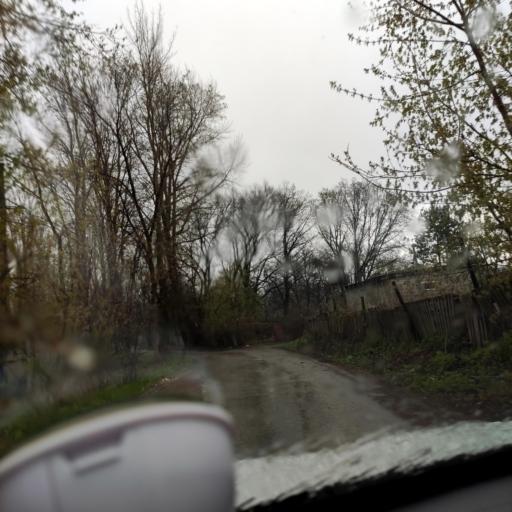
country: RU
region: Samara
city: Novokuybyshevsk
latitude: 53.1417
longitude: 49.9694
